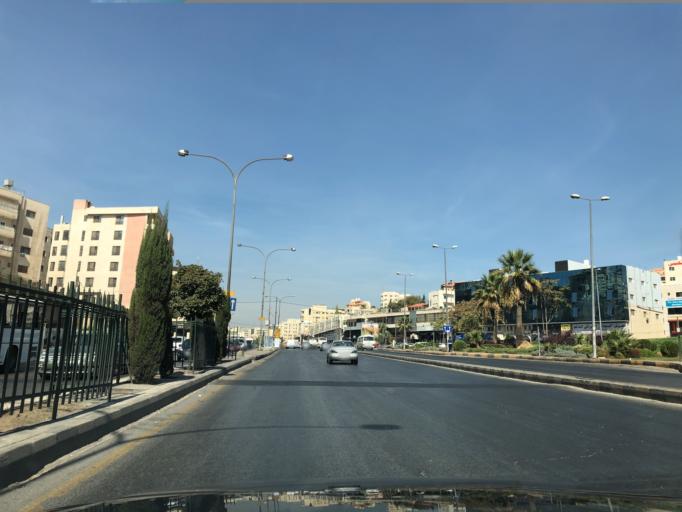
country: JO
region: Amman
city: Al Jubayhah
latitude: 32.0175
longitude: 35.8662
